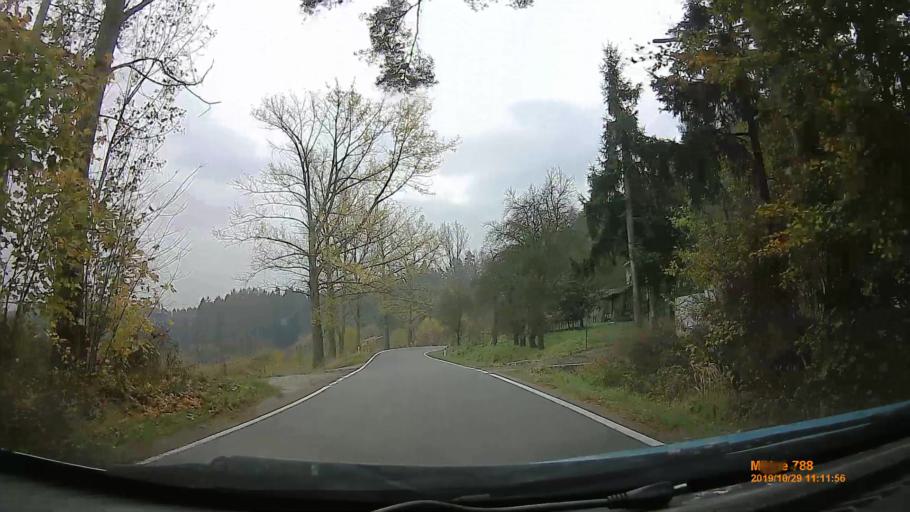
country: PL
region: Lower Silesian Voivodeship
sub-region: Powiat klodzki
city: Polanica-Zdroj
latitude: 50.4312
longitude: 16.5045
